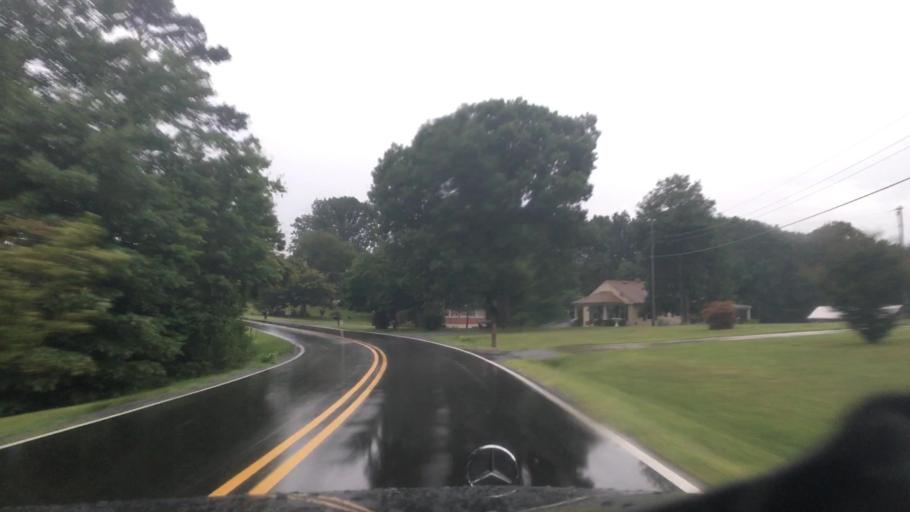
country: US
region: Virginia
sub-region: Campbell County
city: Timberlake
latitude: 37.2856
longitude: -79.2431
